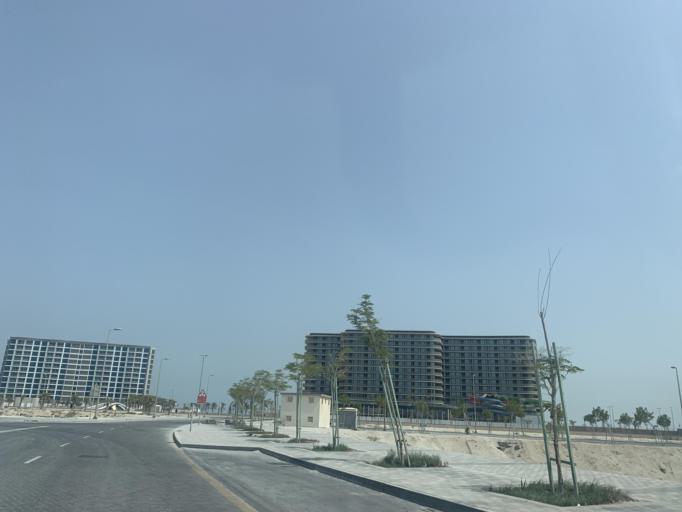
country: BH
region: Muharraq
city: Al Hadd
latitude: 26.2716
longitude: 50.6736
